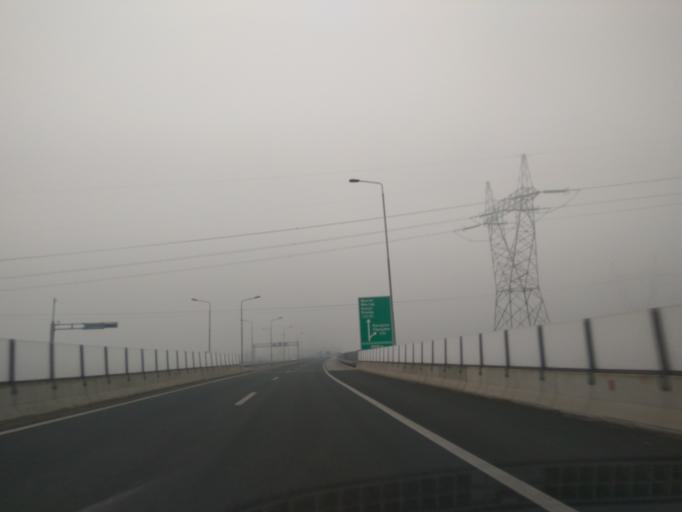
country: BA
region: Federation of Bosnia and Herzegovina
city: Vogosca
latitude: 43.8870
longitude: 18.3117
